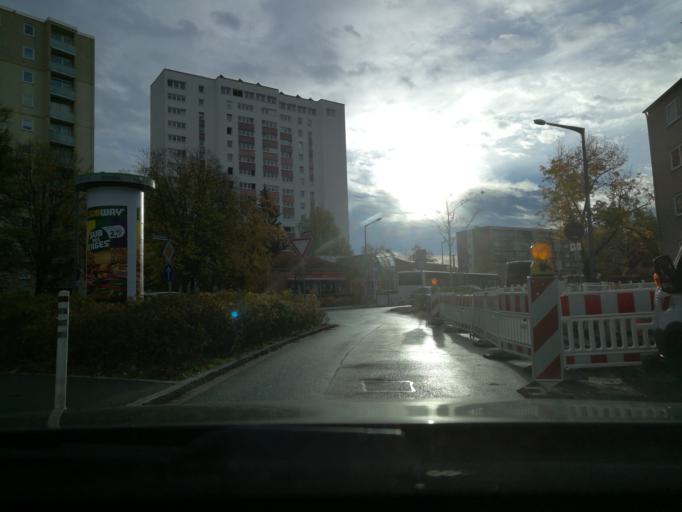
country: DE
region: Bavaria
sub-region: Regierungsbezirk Mittelfranken
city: Furth
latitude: 49.4811
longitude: 10.9553
